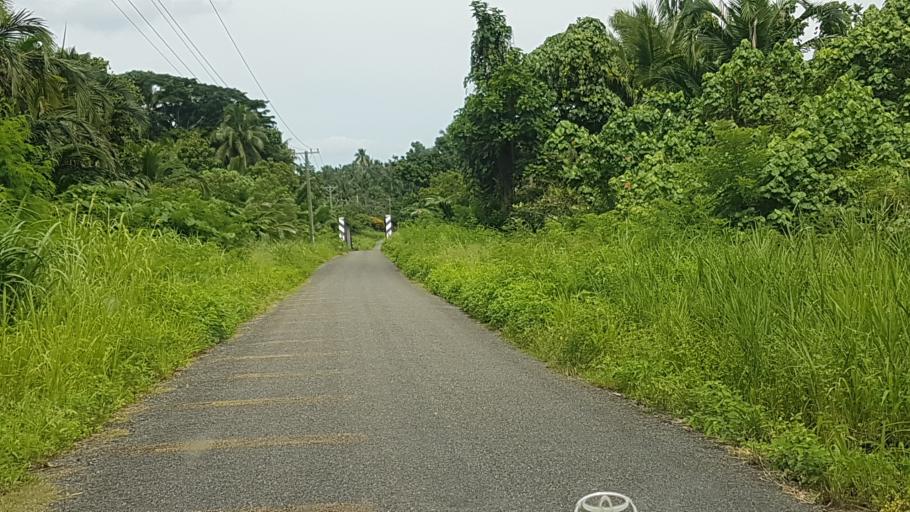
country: PG
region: Madang
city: Madang
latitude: -4.7728
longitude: 145.6909
